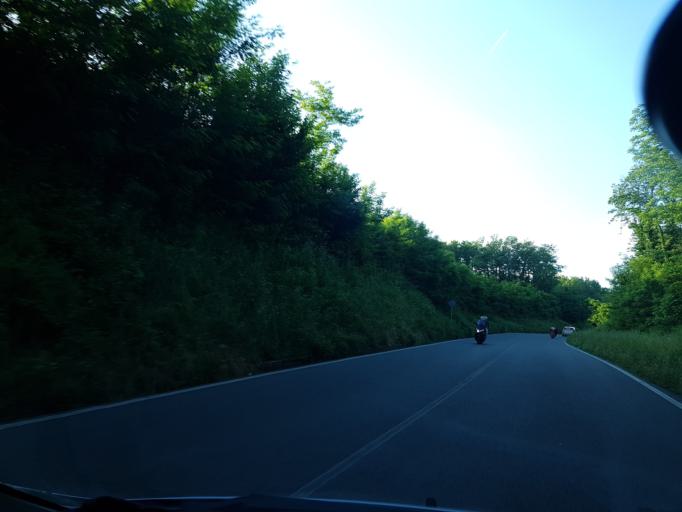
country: IT
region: Tuscany
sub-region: Provincia di Massa-Carrara
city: Fivizzano
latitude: 44.2049
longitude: 10.0836
